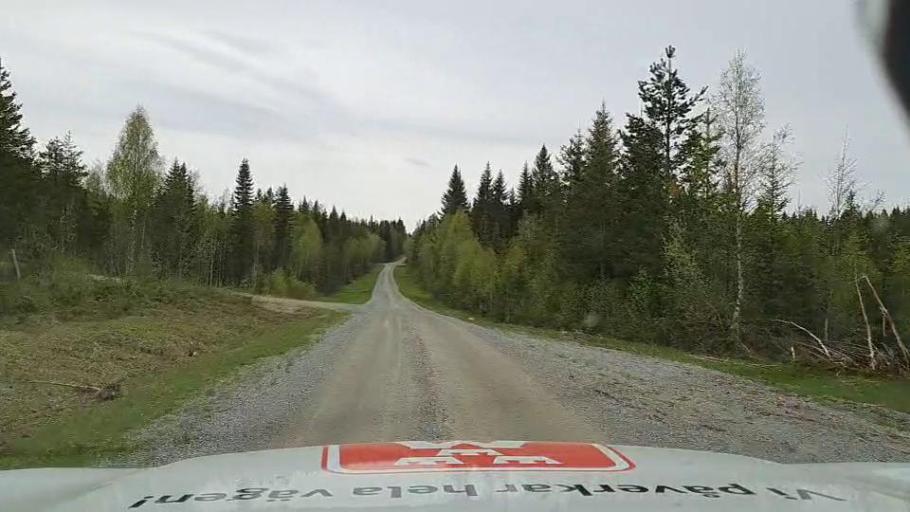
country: SE
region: Jaemtland
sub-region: Bergs Kommun
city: Hoverberg
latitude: 62.5599
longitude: 14.6867
